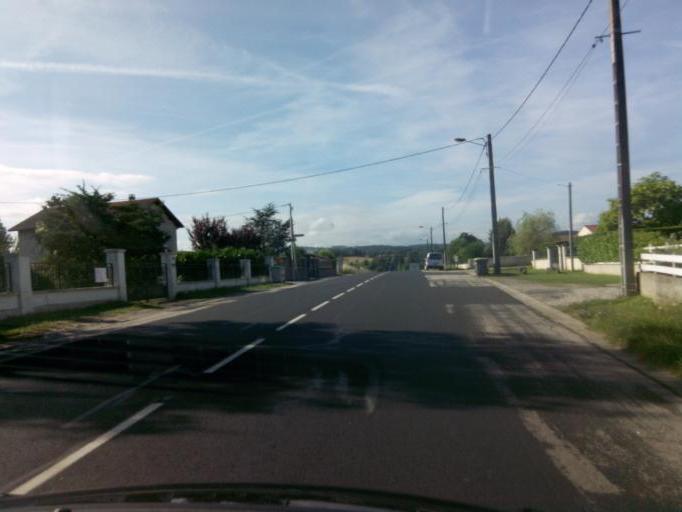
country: FR
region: Auvergne
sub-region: Departement de la Haute-Loire
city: Bas-en-Basset
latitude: 45.2935
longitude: 4.1150
